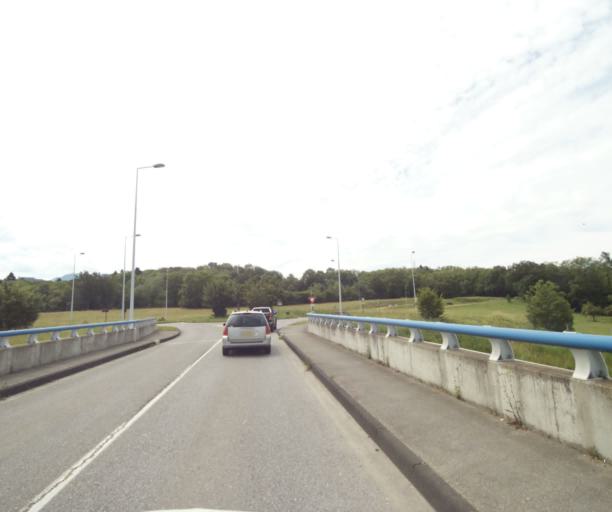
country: FR
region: Rhone-Alpes
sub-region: Departement de la Haute-Savoie
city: Margencel
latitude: 46.3483
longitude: 6.4415
